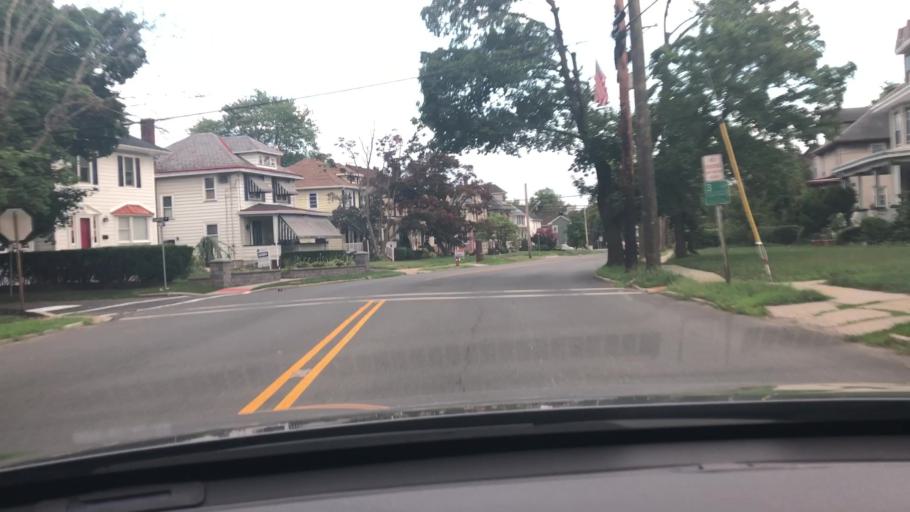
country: US
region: New Jersey
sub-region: Middlesex County
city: Milltown
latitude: 40.4615
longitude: -74.4462
